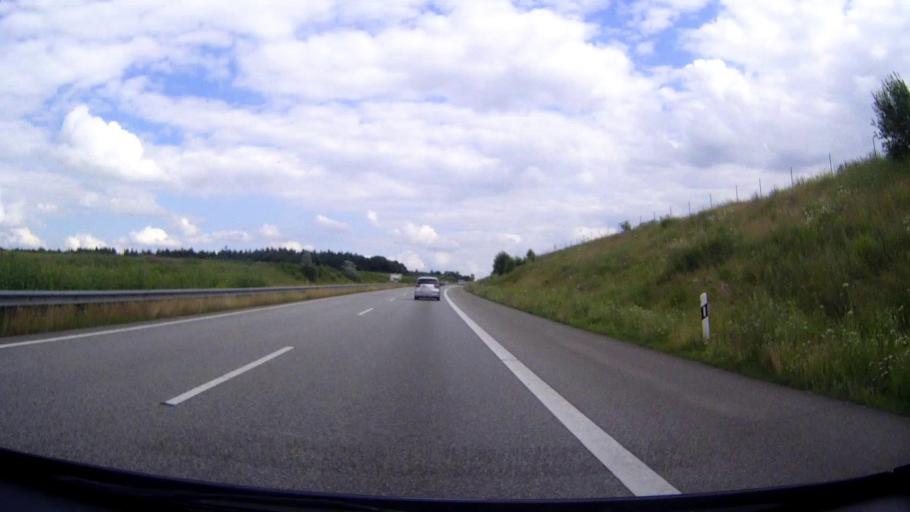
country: DE
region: Schleswig-Holstein
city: Strukdorf
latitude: 53.9229
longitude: 10.4921
